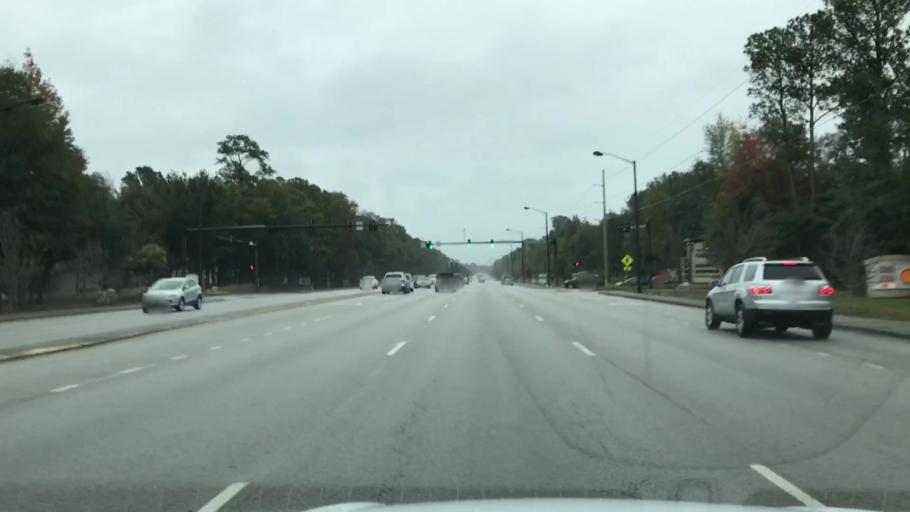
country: US
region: South Carolina
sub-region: Charleston County
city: Isle of Palms
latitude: 32.8642
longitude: -79.7875
